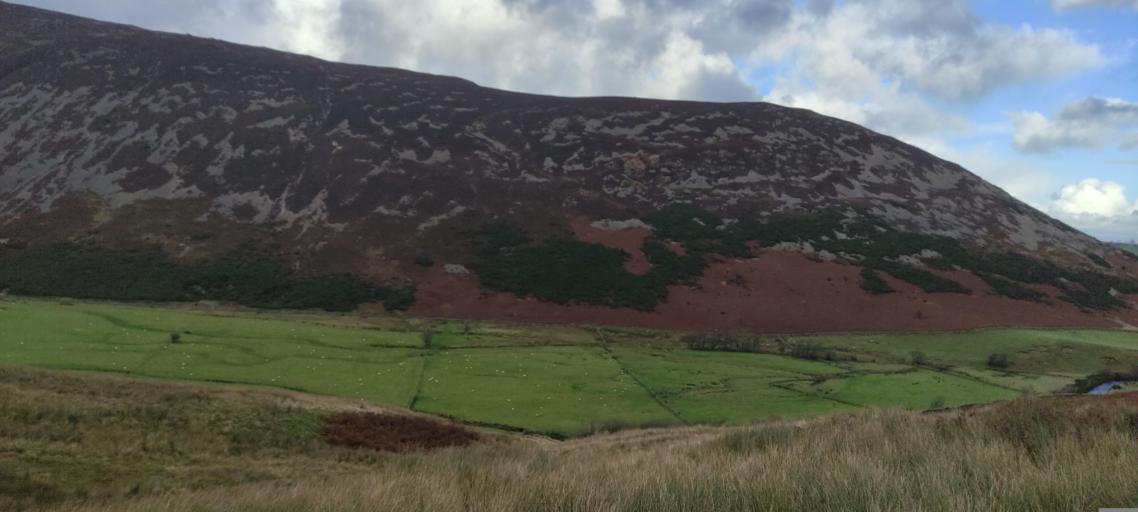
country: GB
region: England
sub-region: Cumbria
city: Keswick
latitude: 54.6760
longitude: -3.0154
